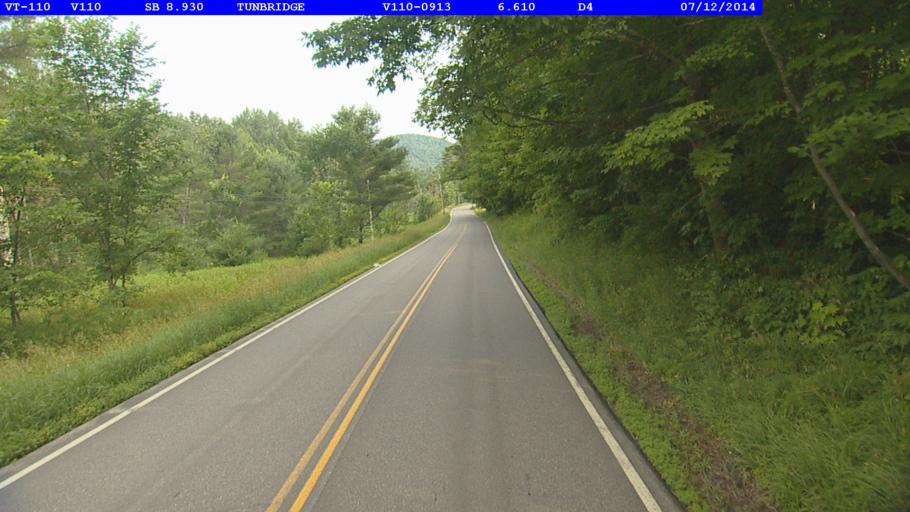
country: US
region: Vermont
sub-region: Orange County
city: Chelsea
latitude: 43.9347
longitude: -72.4666
